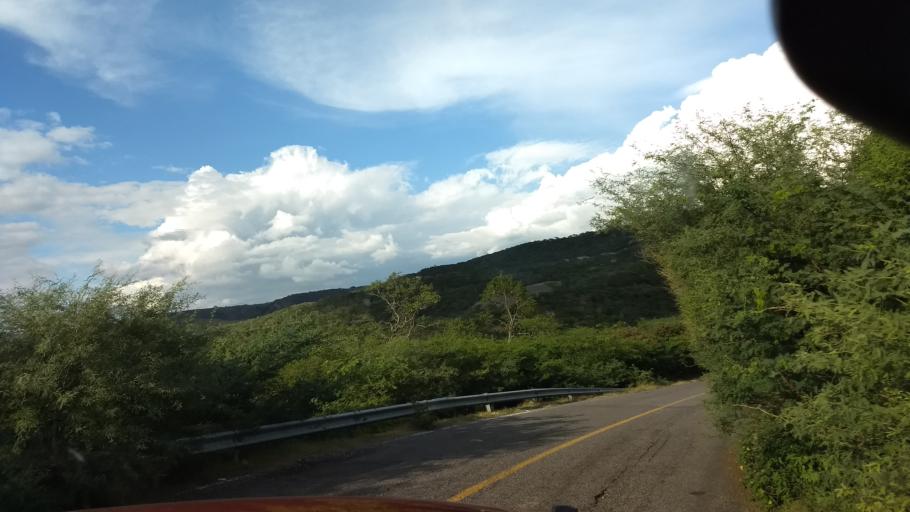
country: MX
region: Colima
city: Suchitlan
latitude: 19.4601
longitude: -103.8278
